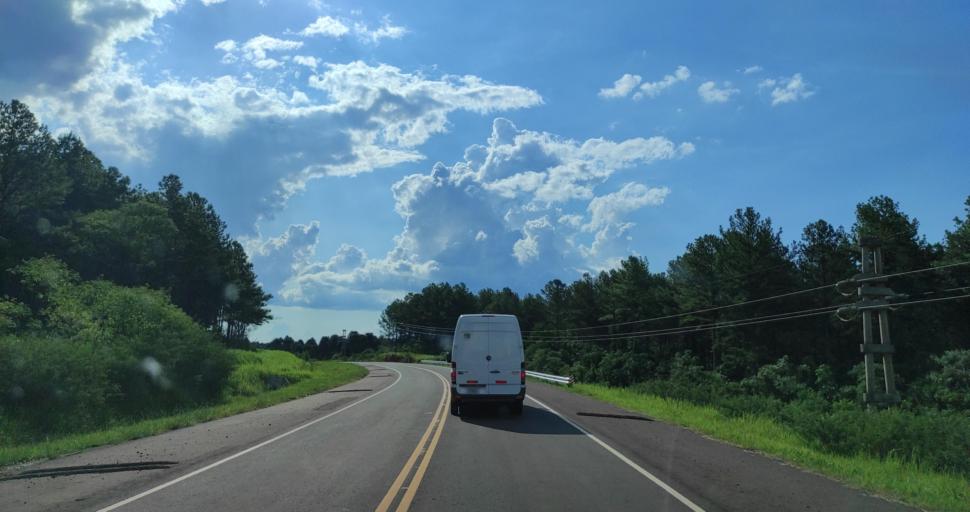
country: AR
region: Misiones
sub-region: Departamento de San Pedro
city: San Pedro
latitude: -26.3481
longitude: -53.9720
